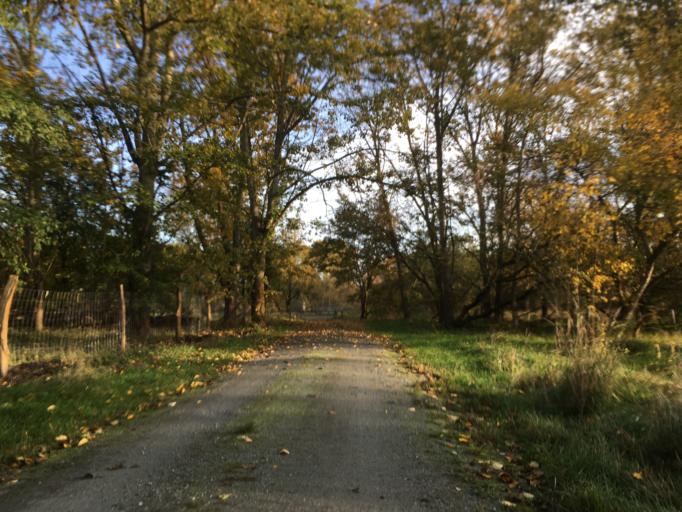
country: DE
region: Berlin
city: Buch
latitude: 52.6451
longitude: 13.4649
